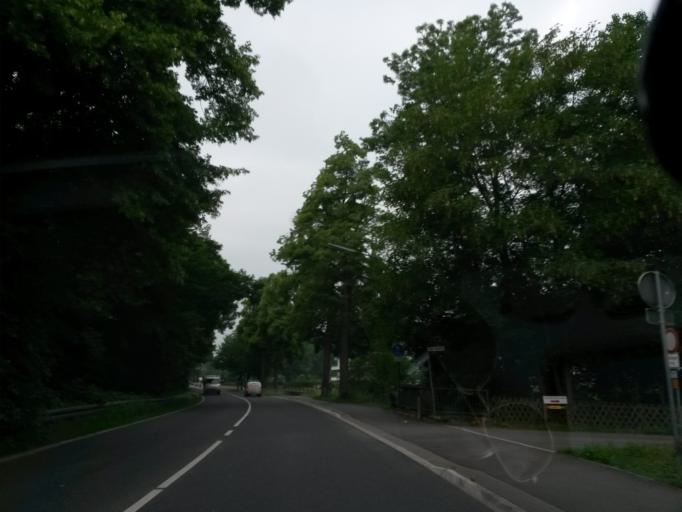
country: DE
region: North Rhine-Westphalia
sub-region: Regierungsbezirk Koln
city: Engelskirchen
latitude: 50.9897
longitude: 7.3955
